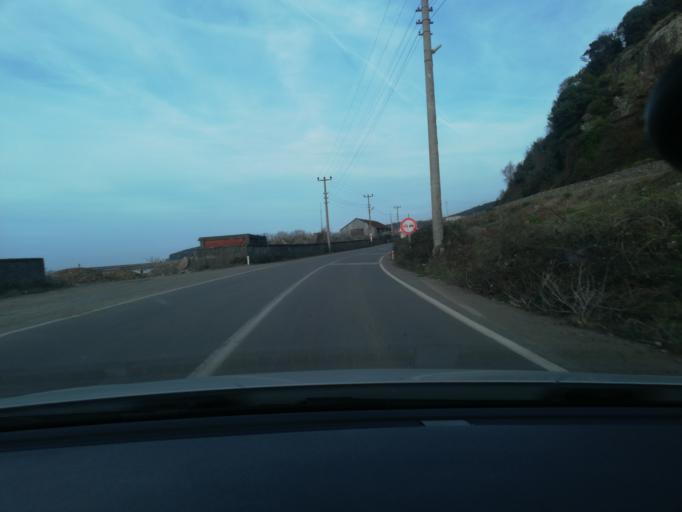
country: TR
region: Zonguldak
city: Tieum
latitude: 41.5570
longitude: 32.0138
